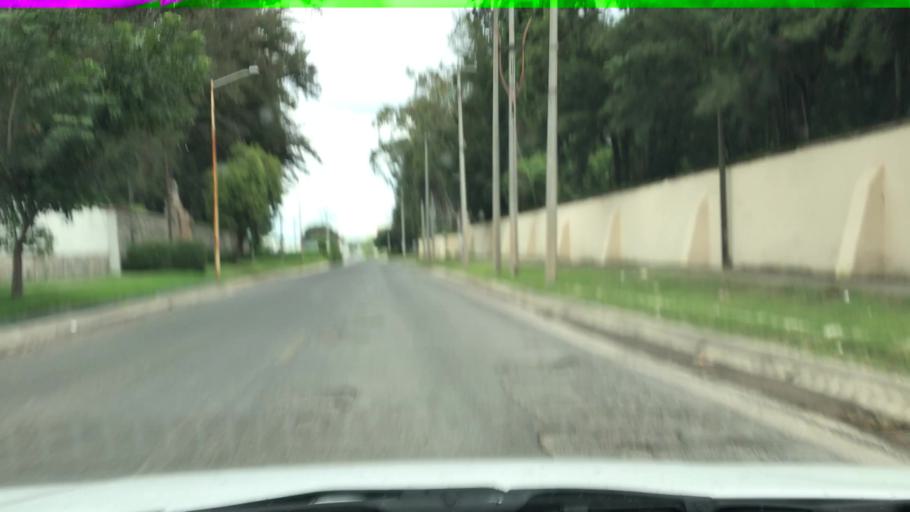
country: MX
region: Jalisco
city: Nicolas R Casillas
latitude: 20.5454
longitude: -103.4838
